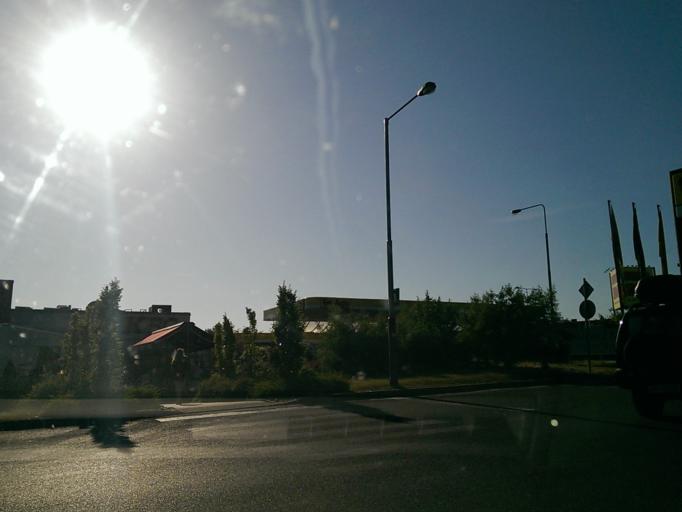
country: CZ
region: Praha
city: Cerny Most
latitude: 50.1101
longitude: 14.5772
